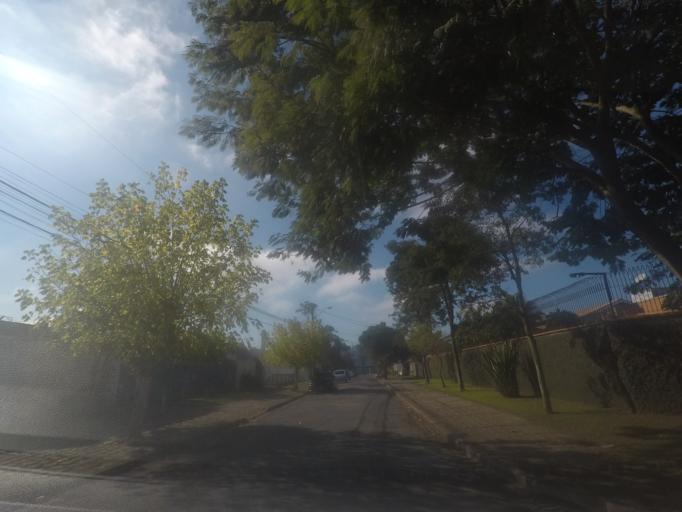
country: BR
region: Parana
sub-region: Pinhais
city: Pinhais
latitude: -25.4576
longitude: -49.2265
